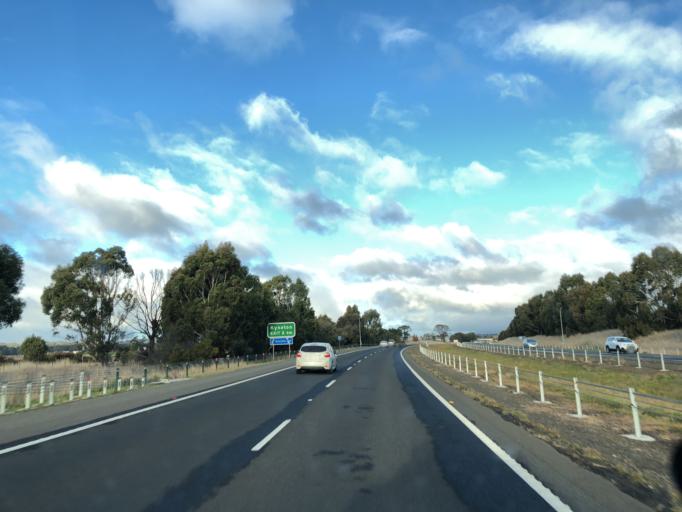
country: AU
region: Victoria
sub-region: Mount Alexander
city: Castlemaine
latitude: -37.2279
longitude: 144.4420
